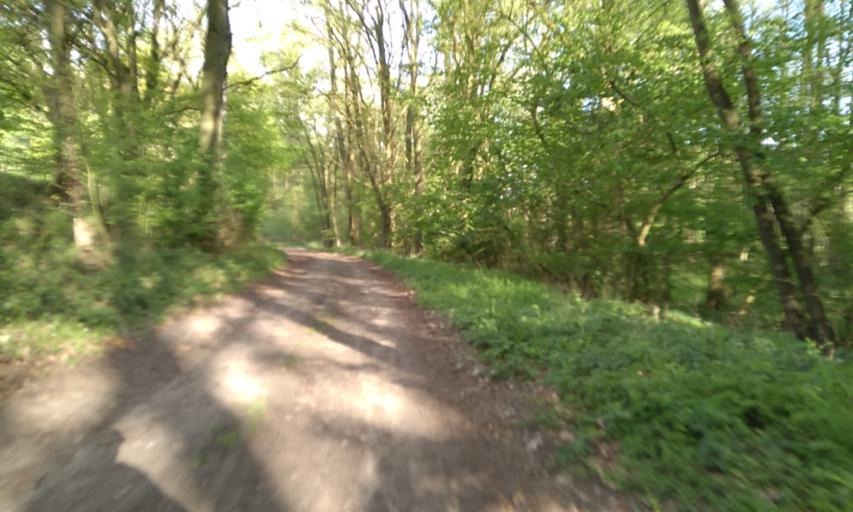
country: DE
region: Lower Saxony
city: Regesbostel
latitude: 53.4102
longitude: 9.6516
